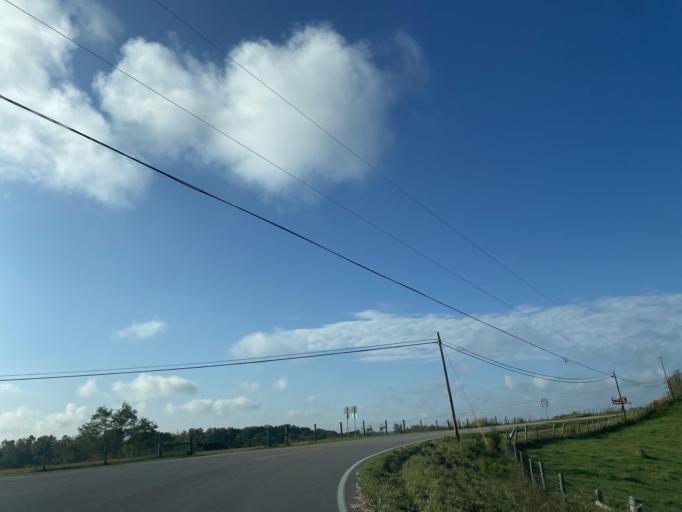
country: US
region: Kentucky
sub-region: Pendleton County
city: Falmouth
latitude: 38.6853
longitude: -84.3128
